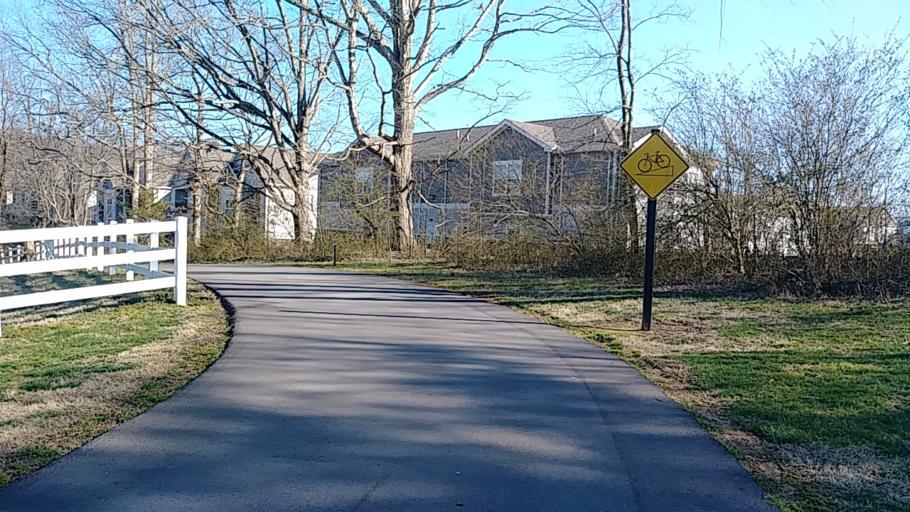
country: US
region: Tennessee
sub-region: Sumner County
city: White House
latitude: 36.4631
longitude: -86.6592
